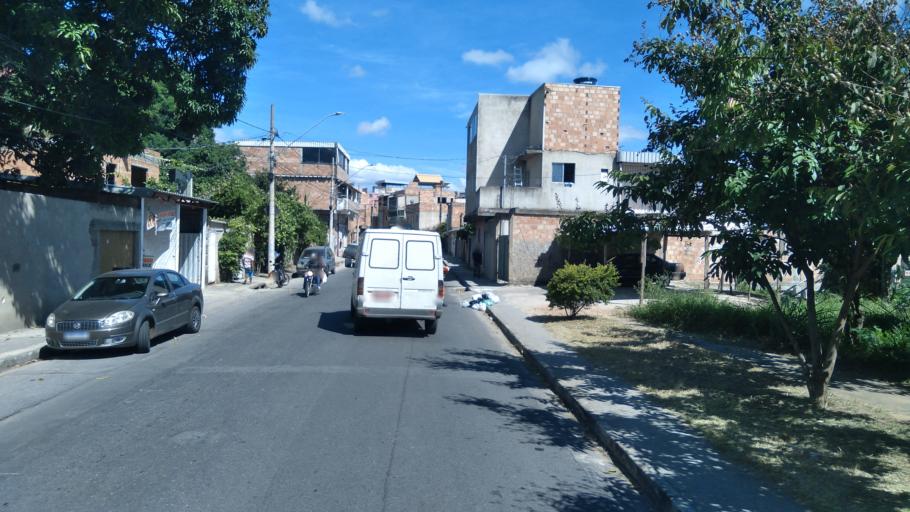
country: BR
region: Minas Gerais
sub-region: Belo Horizonte
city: Belo Horizonte
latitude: -19.8476
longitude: -43.9110
